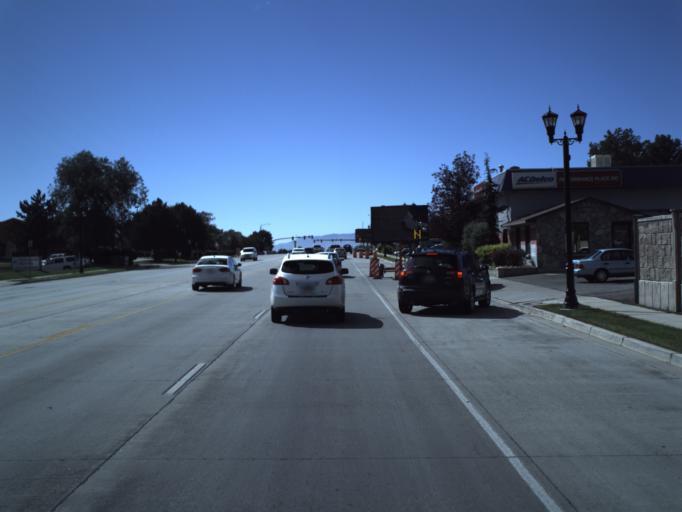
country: US
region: Utah
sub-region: Salt Lake County
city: South Jordan
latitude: 40.5657
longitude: -111.9388
